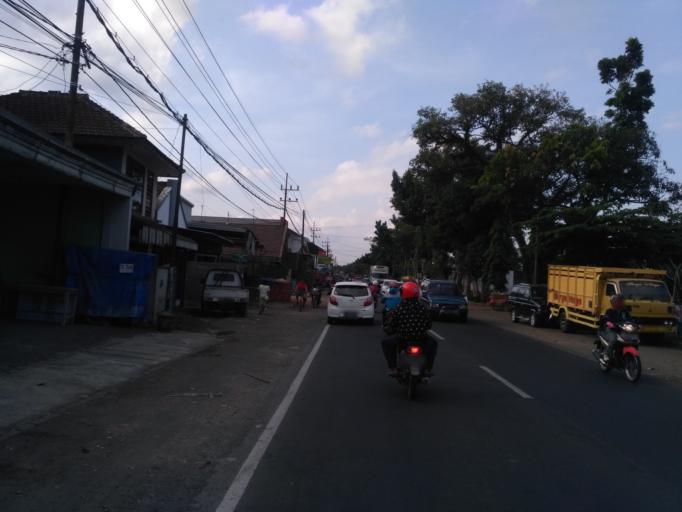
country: ID
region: East Java
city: Golek
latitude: -8.0547
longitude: 112.6041
